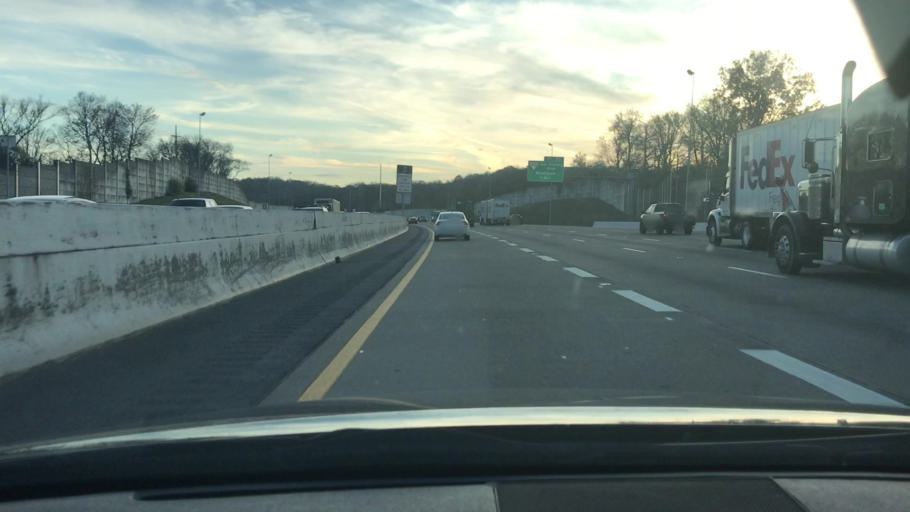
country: US
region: Tennessee
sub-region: Davidson County
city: Goodlettsville
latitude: 36.2827
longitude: -86.7312
